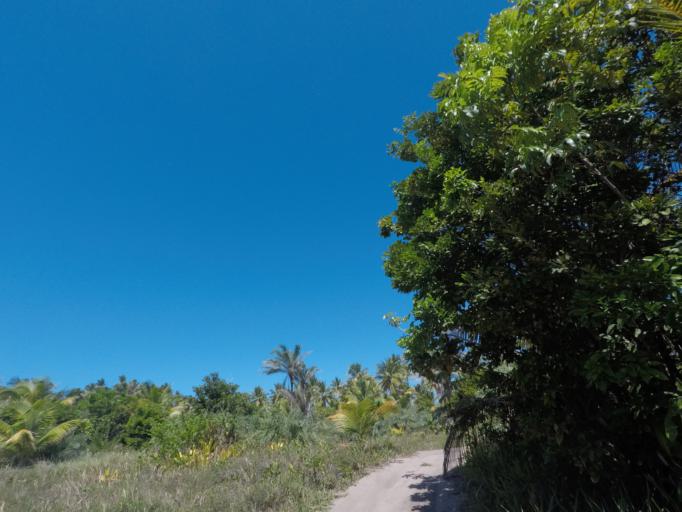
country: BR
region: Bahia
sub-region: Marau
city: Marau
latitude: -13.9614
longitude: -38.9350
